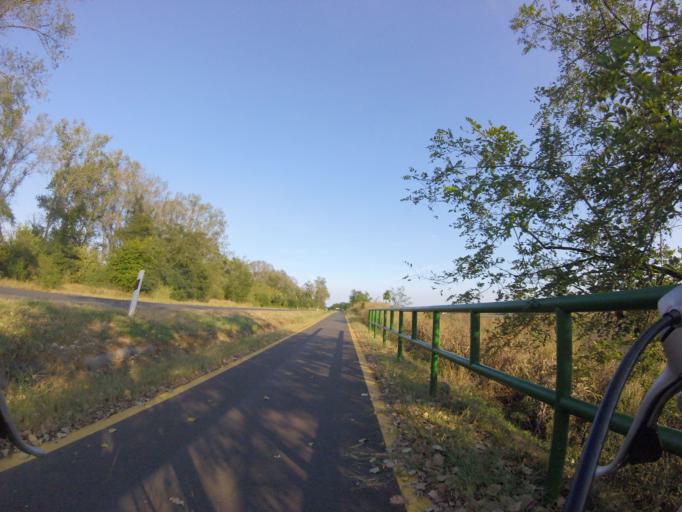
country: HU
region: Szabolcs-Szatmar-Bereg
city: Tiszanagyfalu
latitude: 48.0591
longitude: 21.5528
